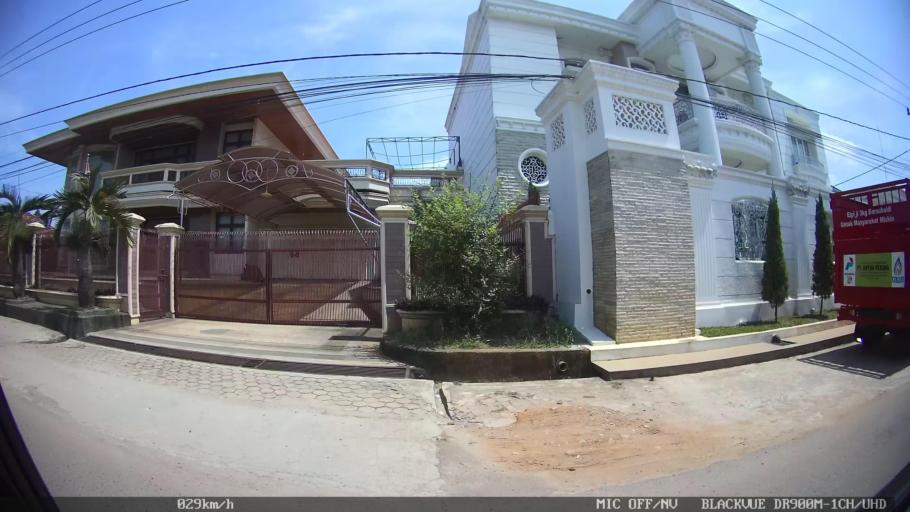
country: ID
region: Lampung
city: Kedaton
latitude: -5.3838
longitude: 105.2746
